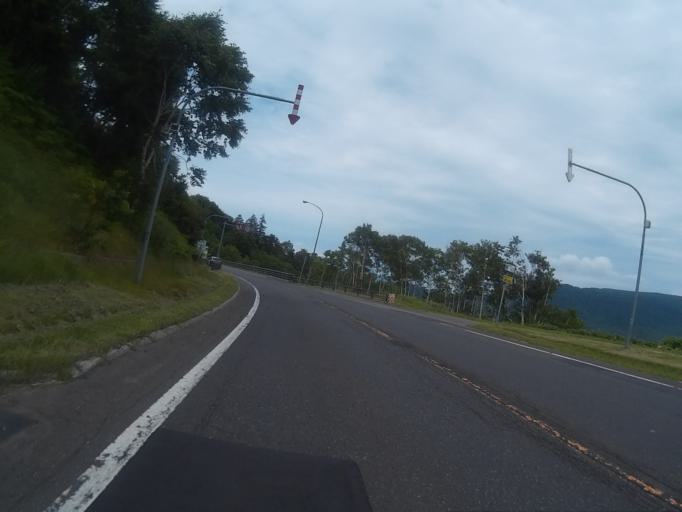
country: JP
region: Hokkaido
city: Sapporo
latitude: 42.8754
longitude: 141.1462
